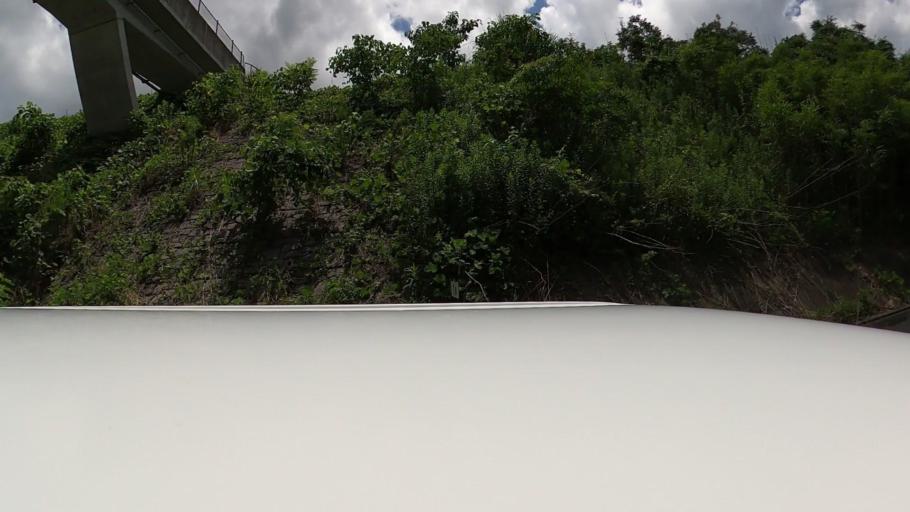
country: JP
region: Miyazaki
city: Nobeoka
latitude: 32.5854
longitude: 131.5130
